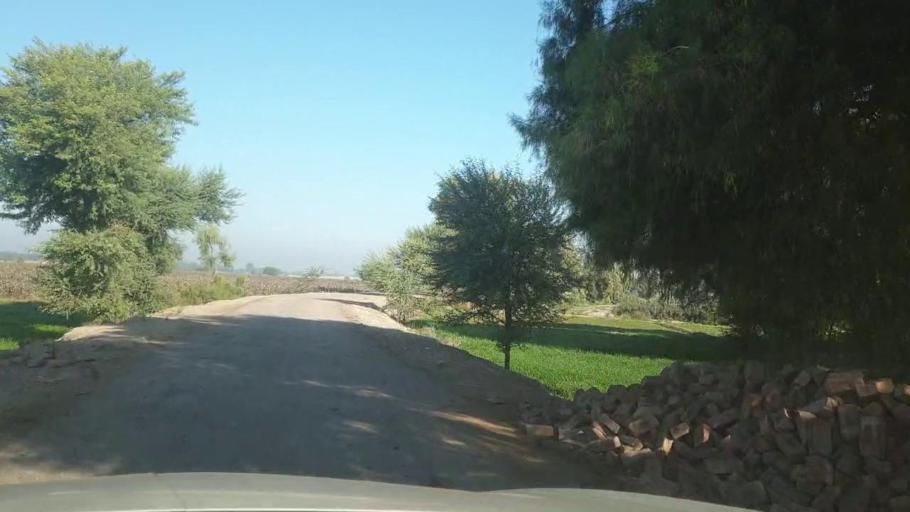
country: PK
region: Sindh
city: Bhan
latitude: 26.5416
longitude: 67.6889
